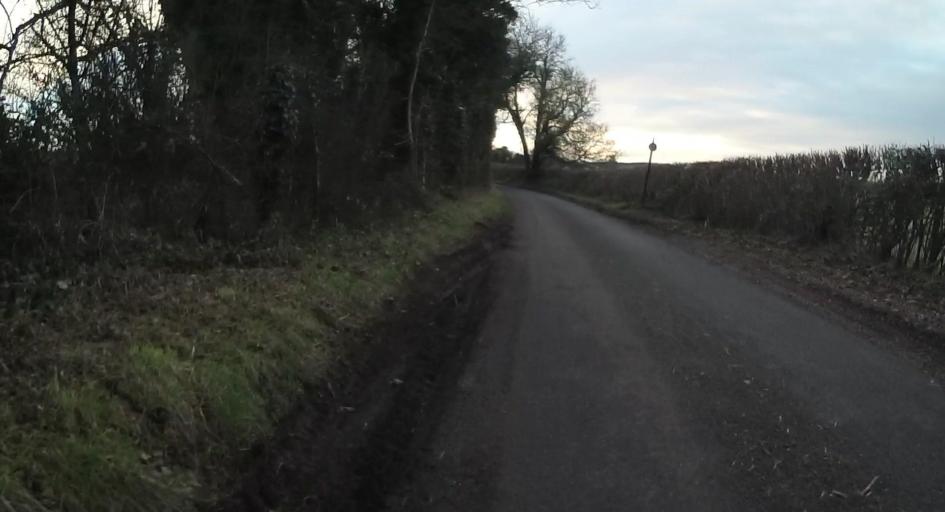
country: GB
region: England
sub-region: Hampshire
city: Swanmore
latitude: 51.0264
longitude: -1.1575
